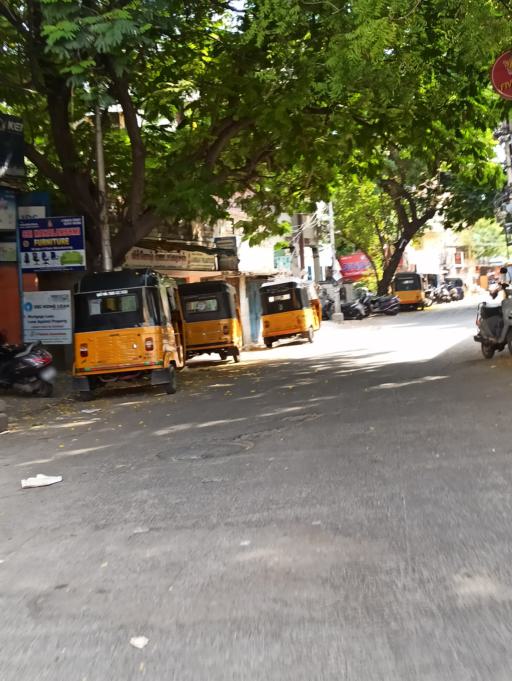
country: IN
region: Tamil Nadu
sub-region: Chennai
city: Chetput
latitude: 13.0598
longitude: 80.2207
